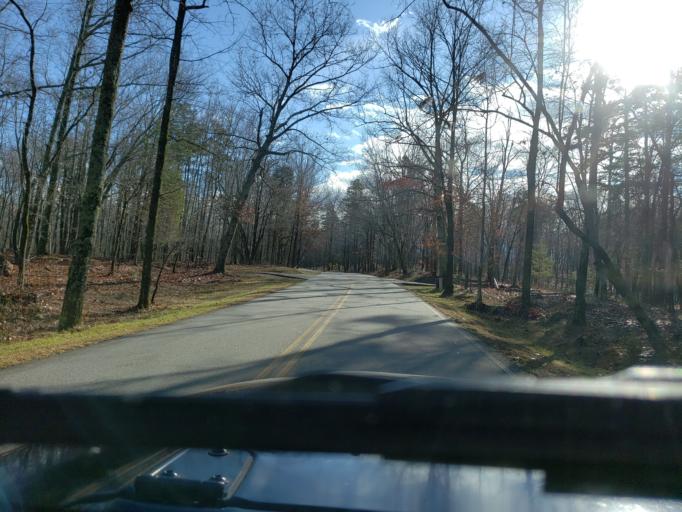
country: US
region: North Carolina
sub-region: Cleveland County
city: White Plains
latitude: 35.1462
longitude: -81.3877
